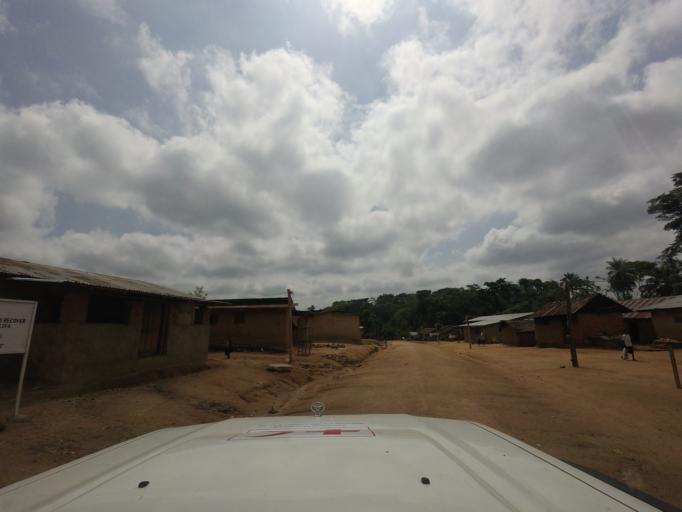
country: LR
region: Lofa
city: Voinjama
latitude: 8.4272
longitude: -9.6709
